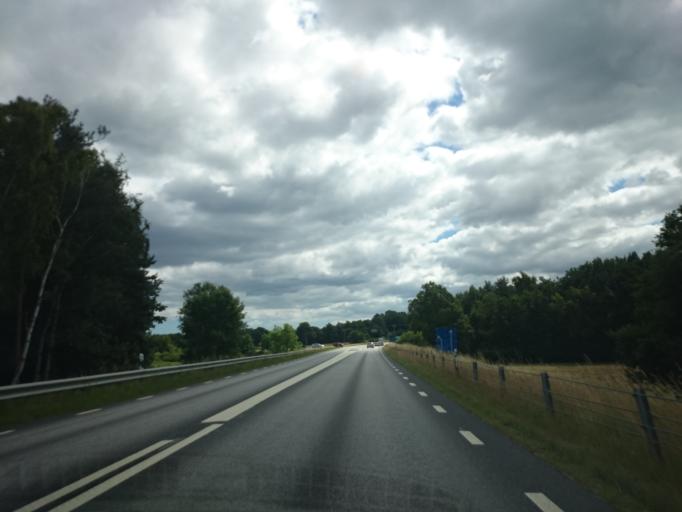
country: SE
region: Skane
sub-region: Kristianstads Kommun
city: Degeberga
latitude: 55.8070
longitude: 14.1441
